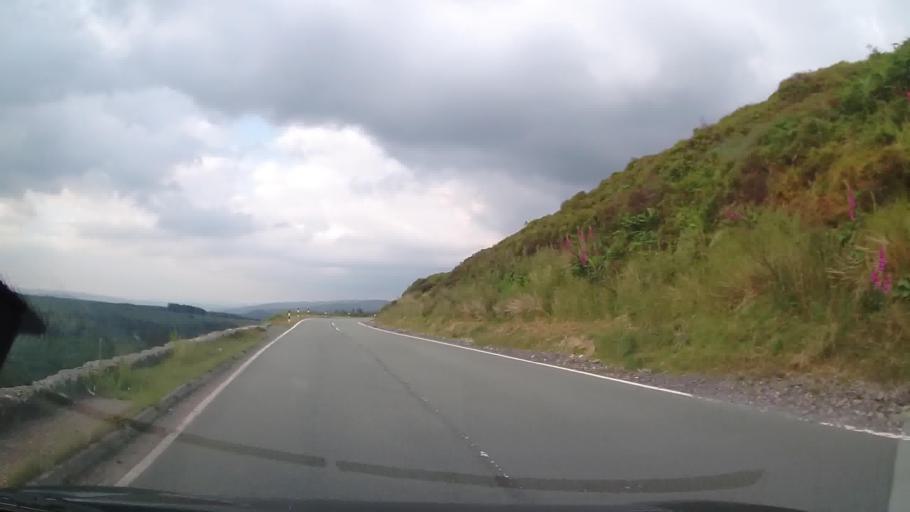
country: GB
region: Wales
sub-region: Denbighshire
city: Llandrillo
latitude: 52.8713
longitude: -3.4735
